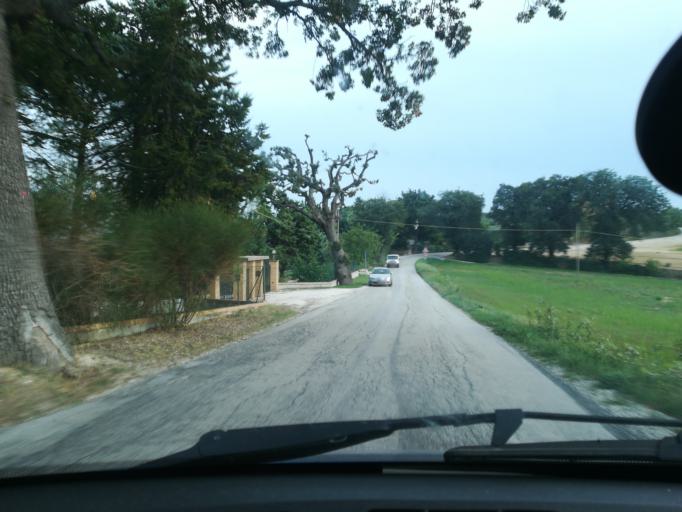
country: IT
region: The Marches
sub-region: Provincia di Macerata
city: Piediripa
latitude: 43.3024
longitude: 13.4792
